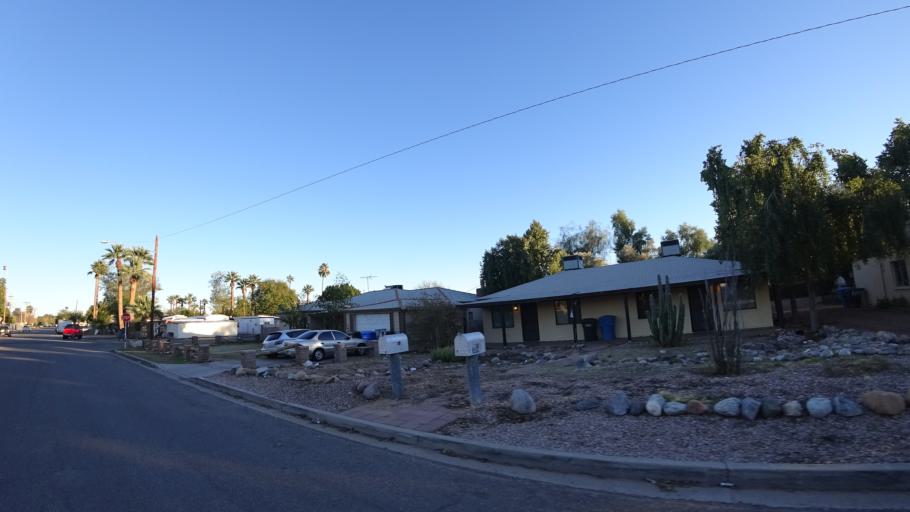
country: US
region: Arizona
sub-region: Maricopa County
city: Phoenix
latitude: 33.4767
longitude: -112.0156
